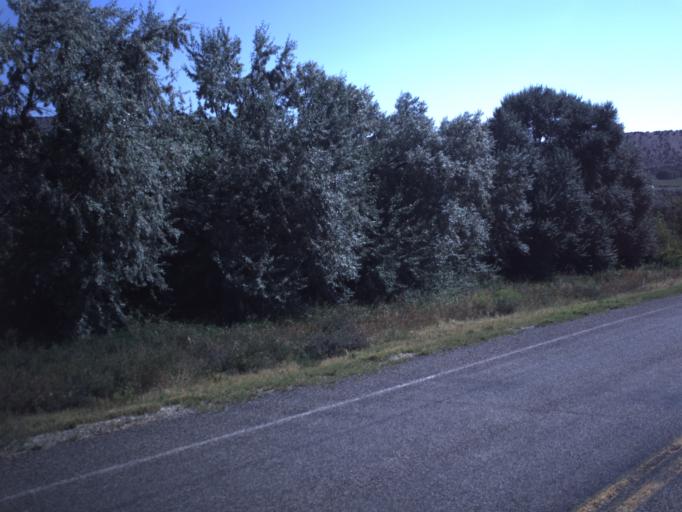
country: US
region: Utah
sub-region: Duchesne County
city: Duchesne
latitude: 40.2706
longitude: -110.4478
